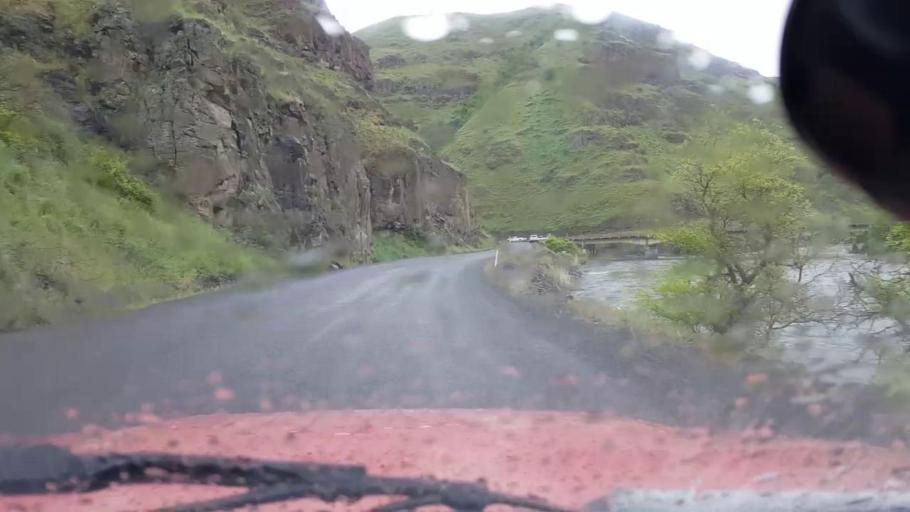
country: US
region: Washington
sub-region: Asotin County
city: Asotin
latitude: 46.0431
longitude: -117.2539
